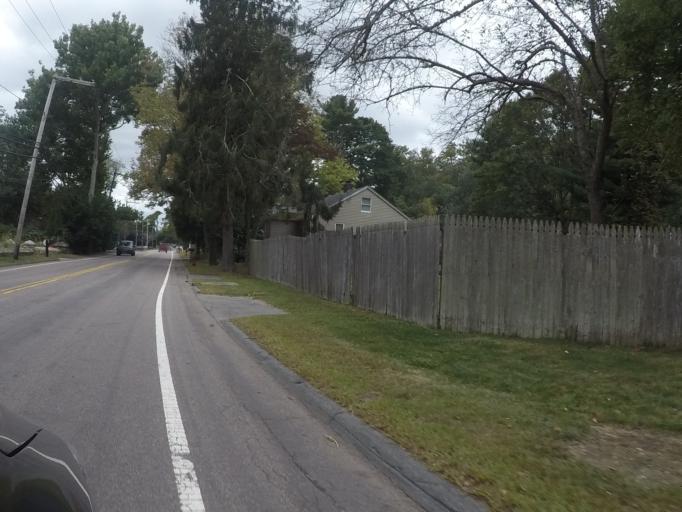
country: US
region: Massachusetts
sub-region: Bristol County
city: Smith Mills
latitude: 41.6319
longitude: -70.9916
